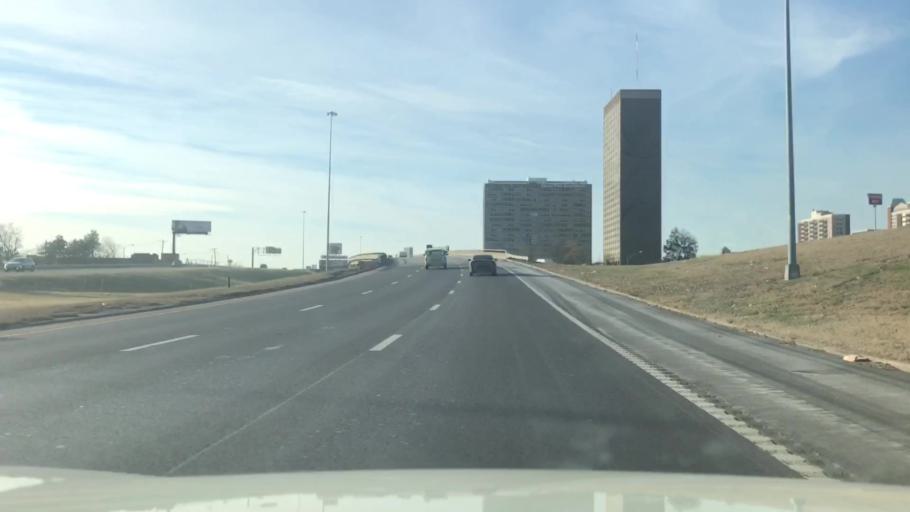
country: US
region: Missouri
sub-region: City of Saint Louis
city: St. Louis
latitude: 38.6306
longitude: -90.2277
